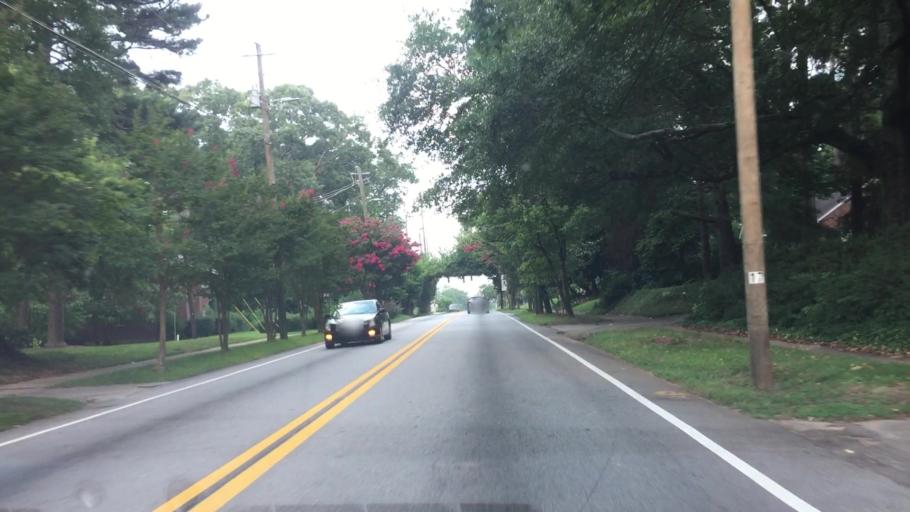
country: US
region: Georgia
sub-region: DeKalb County
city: Avondale Estates
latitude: 33.7752
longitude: -84.2638
